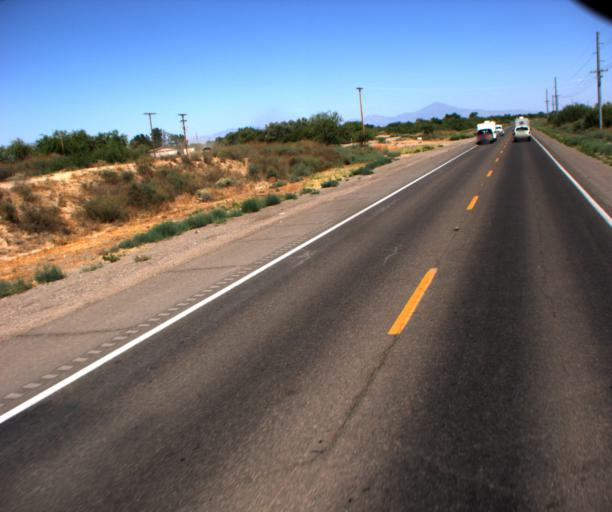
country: US
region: Arizona
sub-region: Graham County
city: Pima
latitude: 32.9363
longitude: -109.8994
